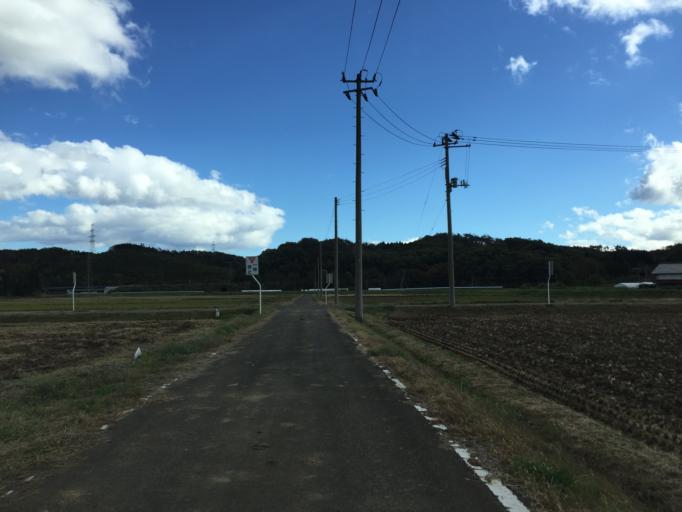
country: JP
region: Fukushima
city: Nihommatsu
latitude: 37.6592
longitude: 140.4299
